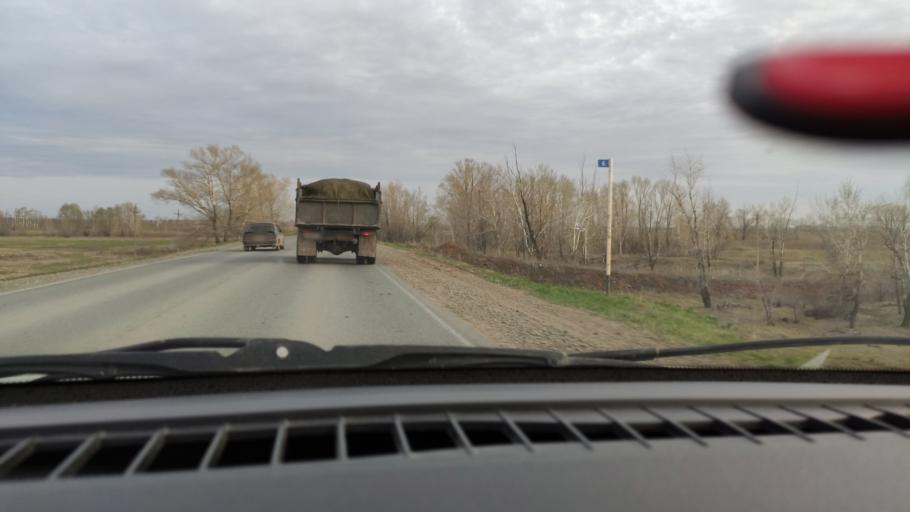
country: RU
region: Orenburg
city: Tatarskaya Kargala
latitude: 51.9187
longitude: 55.1735
